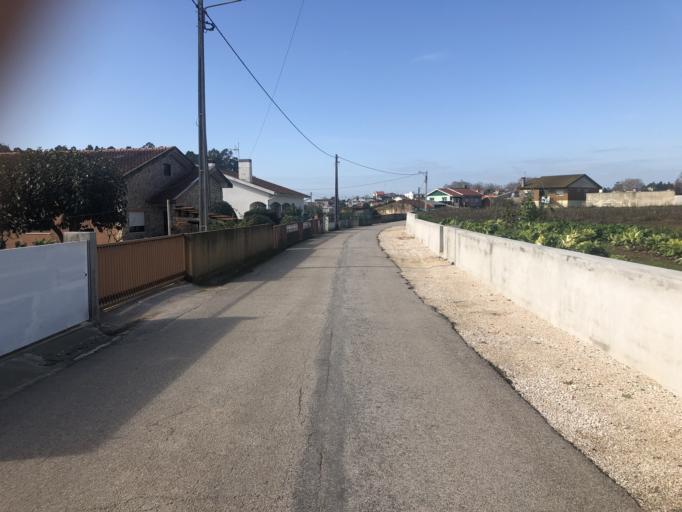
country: PT
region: Aveiro
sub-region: Estarreja
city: Beduido
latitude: 40.7669
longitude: -8.5461
